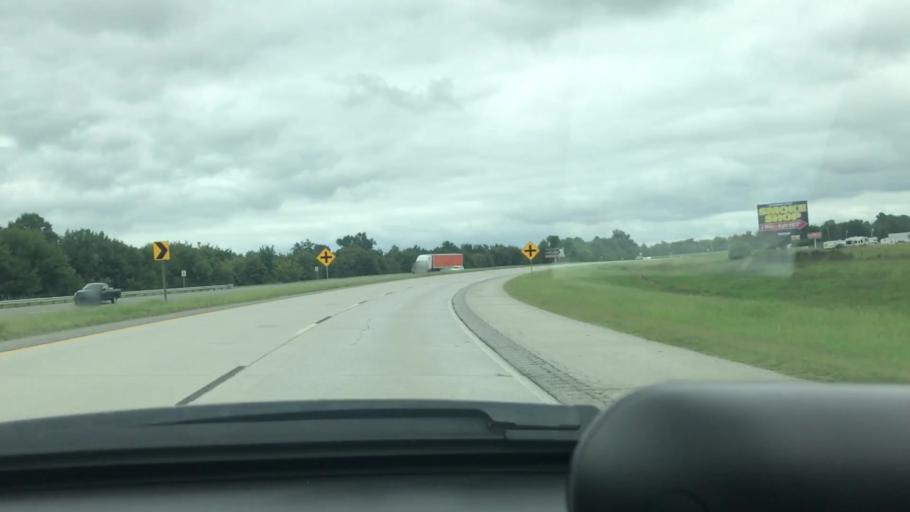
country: US
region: Oklahoma
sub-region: Wagoner County
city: Wagoner
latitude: 35.9123
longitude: -95.4017
